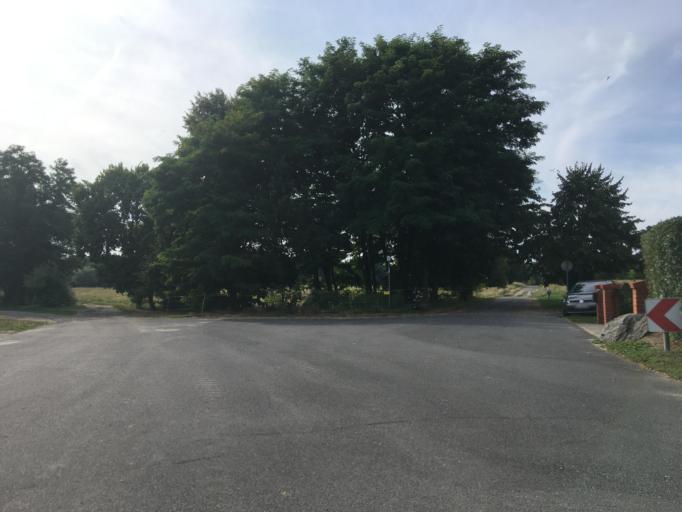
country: DE
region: Brandenburg
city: Eberswalde
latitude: 52.7822
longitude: 13.8323
